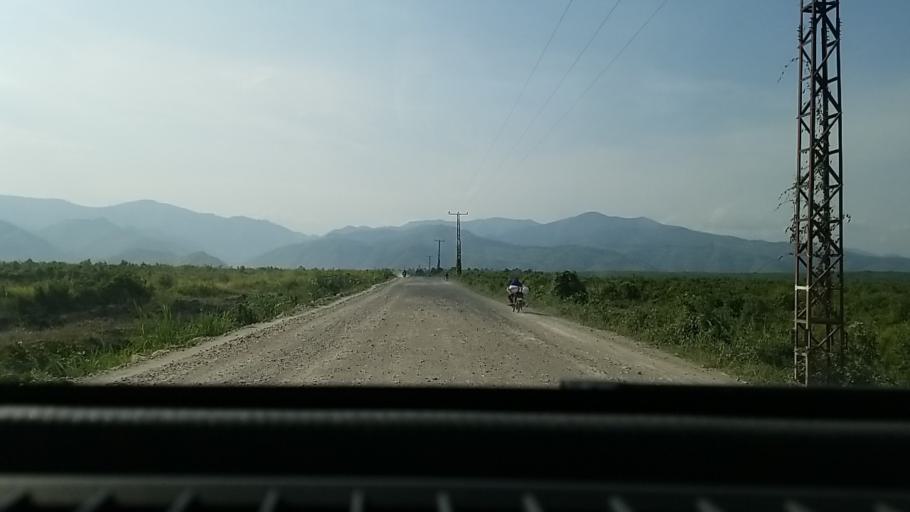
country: CD
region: Nord Kivu
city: Sake
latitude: -1.5815
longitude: 29.0808
